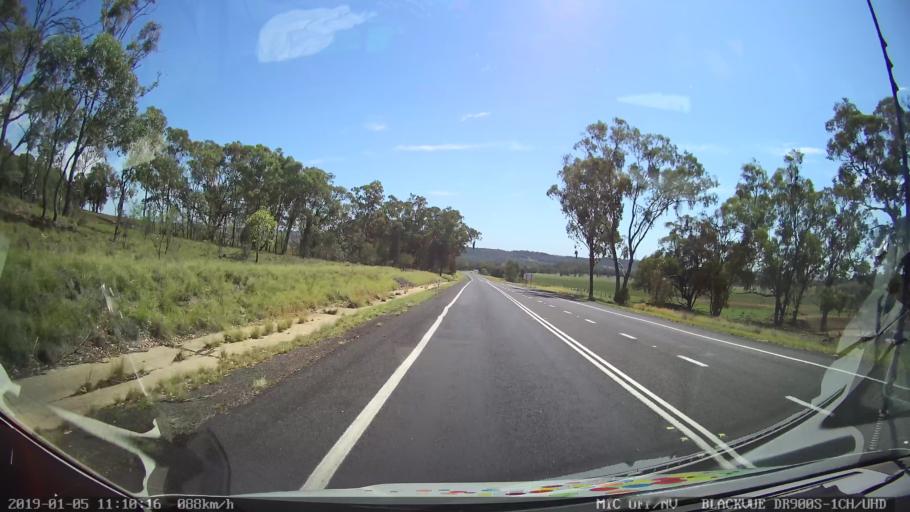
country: AU
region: New South Wales
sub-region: Warrumbungle Shire
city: Coonabarabran
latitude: -31.4082
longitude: 149.2427
